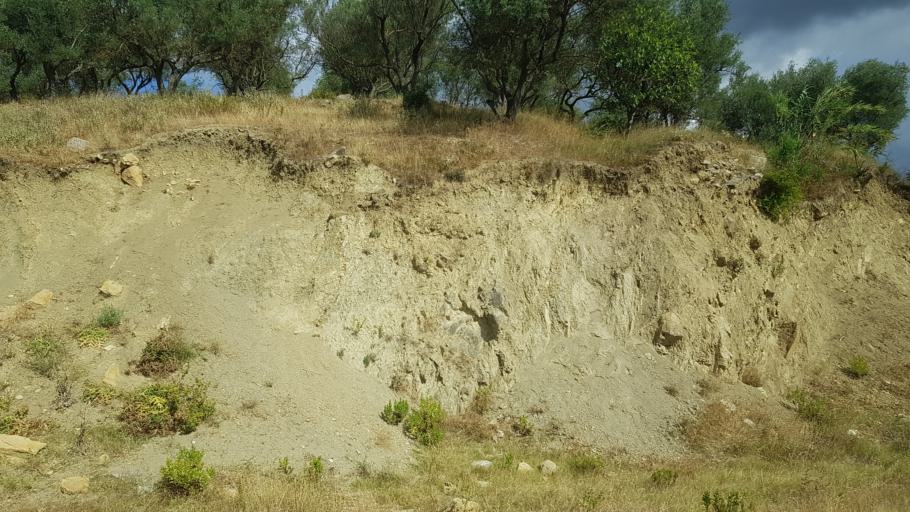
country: AL
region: Vlore
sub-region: Rrethi i Delvines
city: Mesopotam
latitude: 39.9013
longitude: 20.0855
